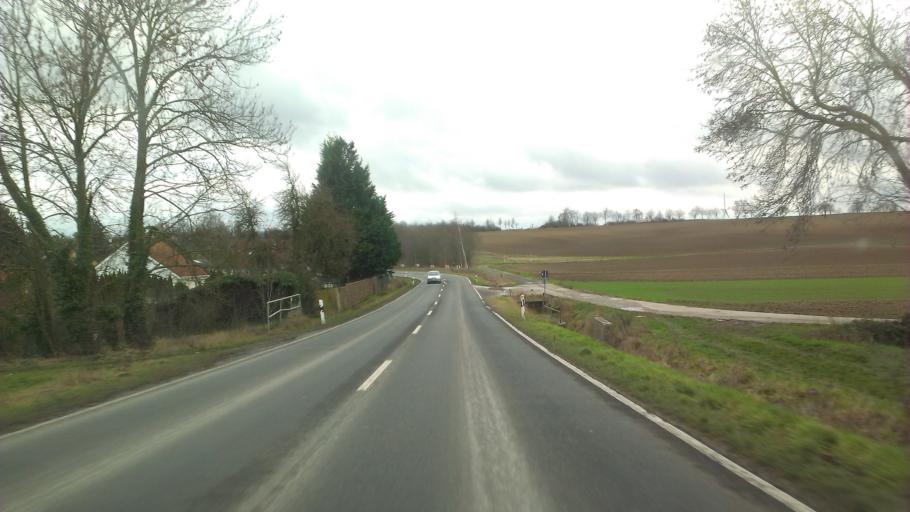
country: DE
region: Rheinland-Pfalz
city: Flomborn
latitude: 49.6949
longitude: 8.1441
